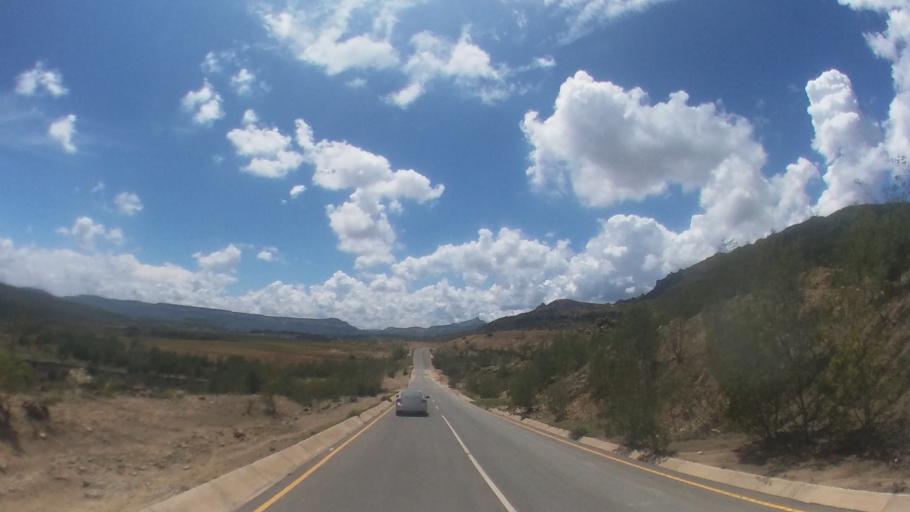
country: LS
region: Maseru
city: Nako
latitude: -29.6244
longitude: 27.5350
